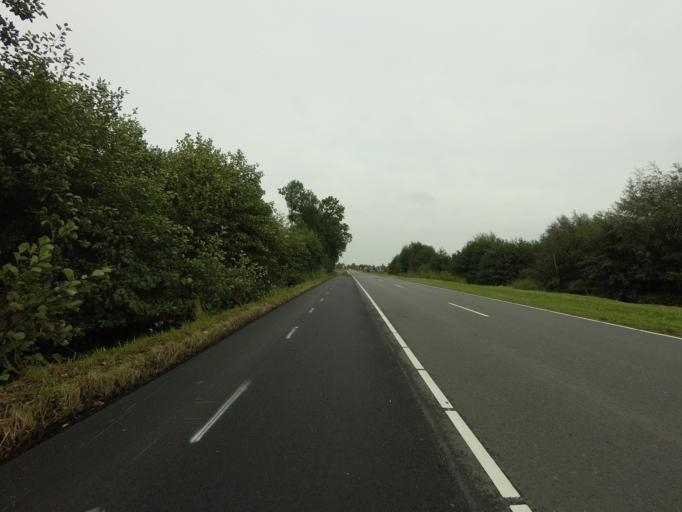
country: NL
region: Utrecht
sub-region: Gemeente De Ronde Venen
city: Mijdrecht
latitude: 52.1461
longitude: 4.8597
